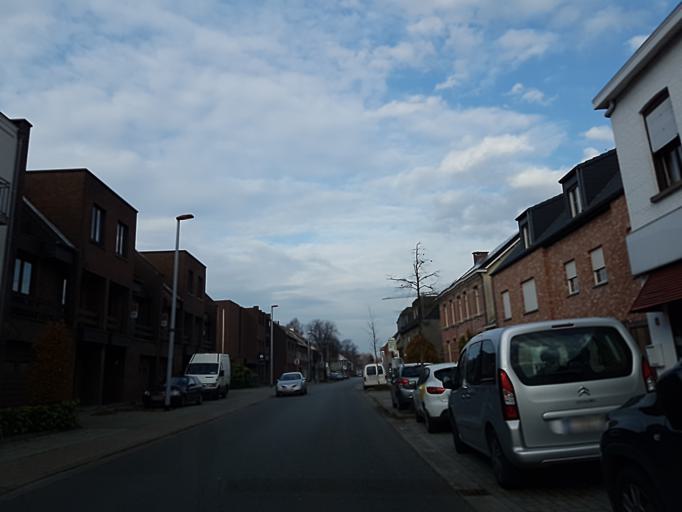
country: BE
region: Flanders
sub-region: Provincie Antwerpen
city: Kalmthout
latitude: 51.3921
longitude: 4.4746
